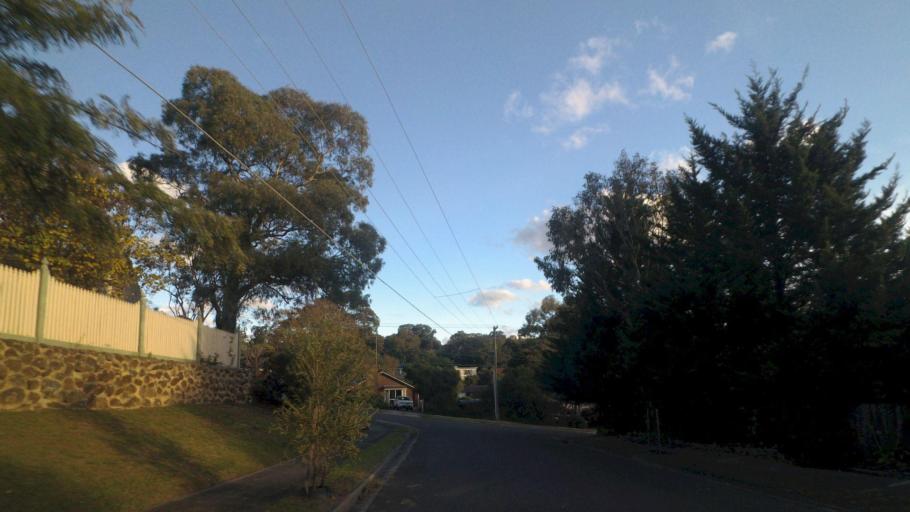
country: AU
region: Victoria
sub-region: Banyule
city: Lower Plenty
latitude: -37.7272
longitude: 145.1199
